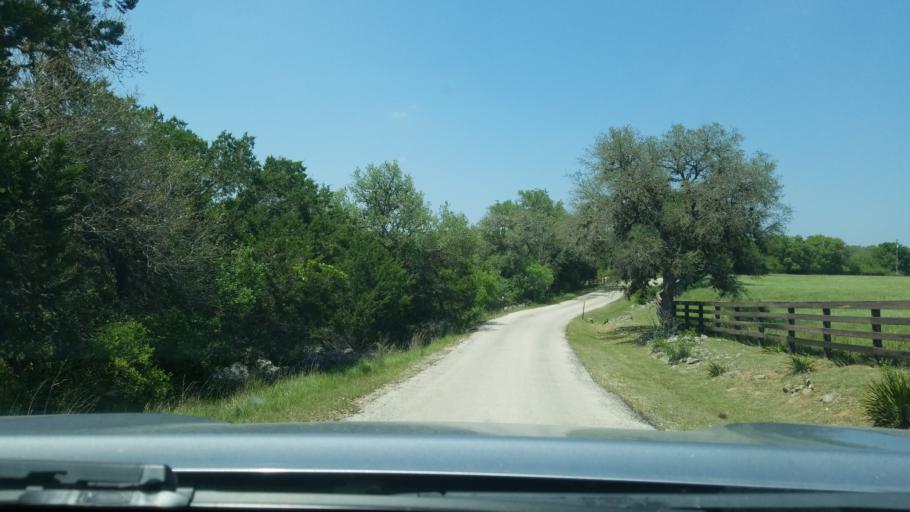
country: US
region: Texas
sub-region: Blanco County
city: Blanco
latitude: 30.0089
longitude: -98.4366
